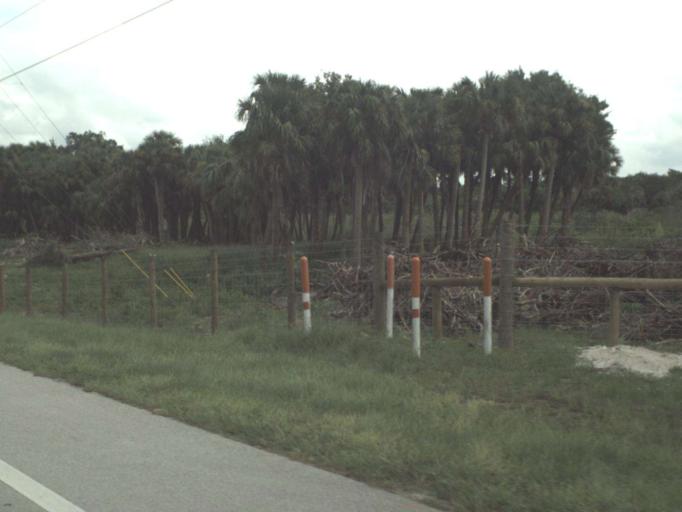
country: US
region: Florida
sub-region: Martin County
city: Indiantown
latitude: 27.0900
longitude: -80.6573
